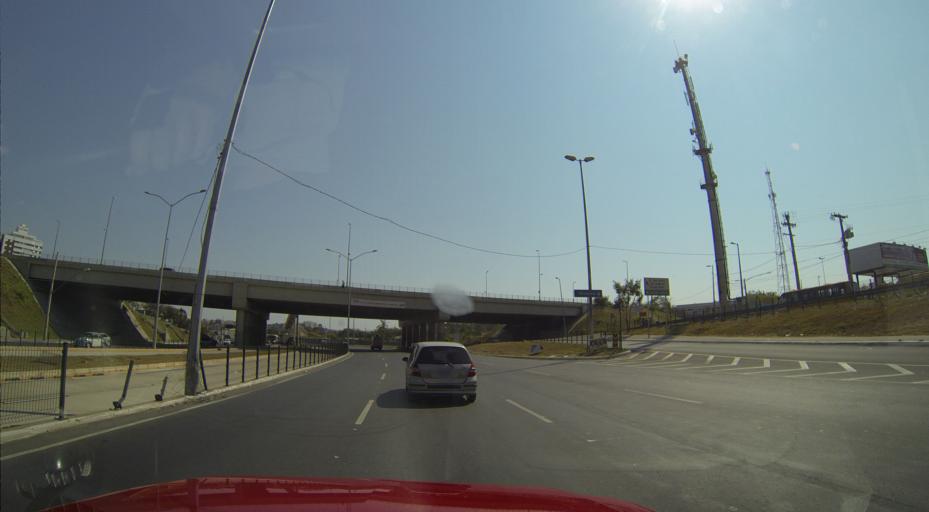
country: BR
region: Minas Gerais
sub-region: Belo Horizonte
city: Belo Horizonte
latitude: -19.8725
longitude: -43.9274
